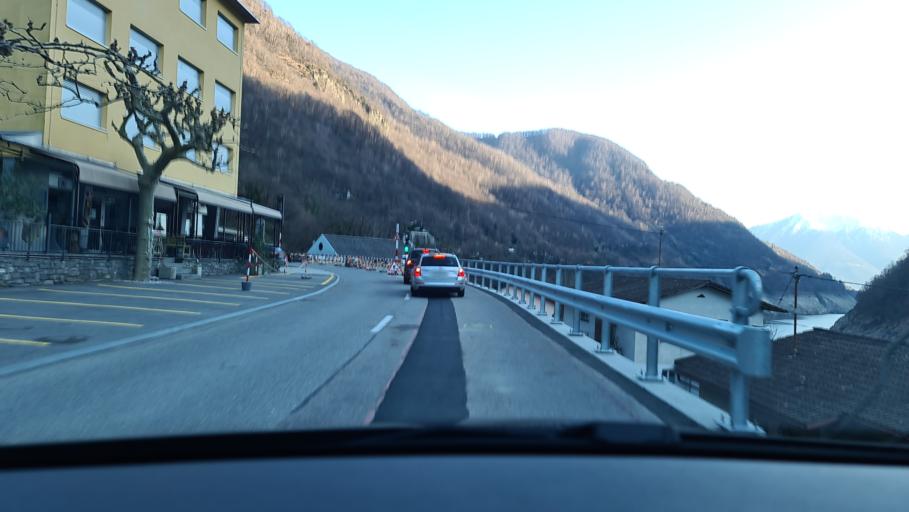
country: CH
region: Ticino
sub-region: Locarno District
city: Gordola
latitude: 46.2220
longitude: 8.8584
